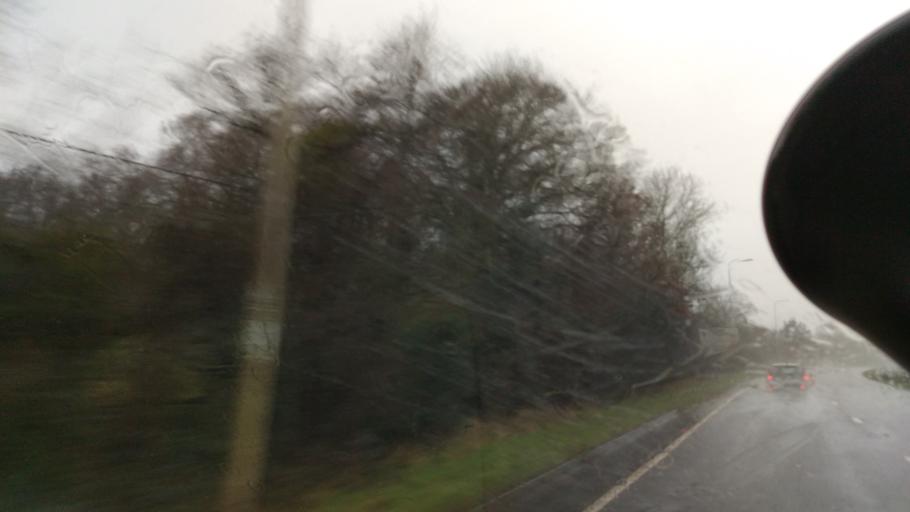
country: GB
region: England
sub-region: West Sussex
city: Fontwell
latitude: 50.8537
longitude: -0.6348
